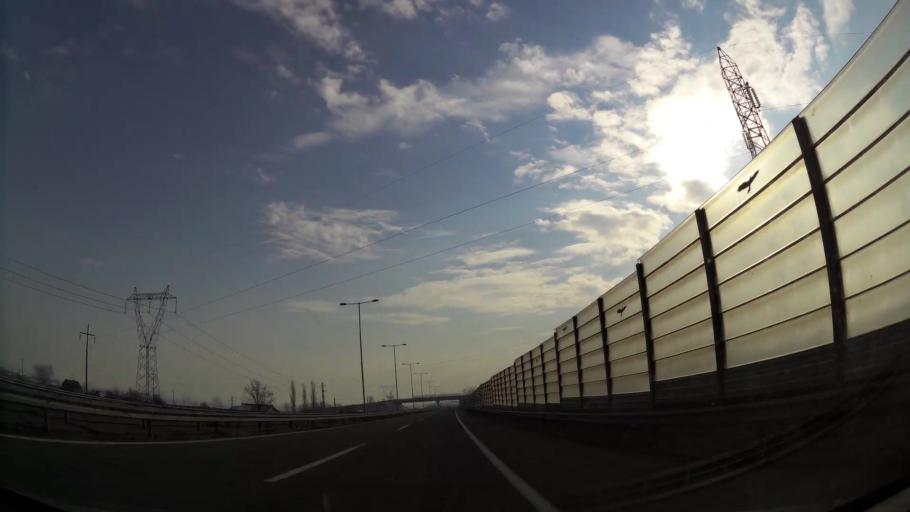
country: MK
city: Creshevo
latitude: 42.0287
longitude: 21.5297
